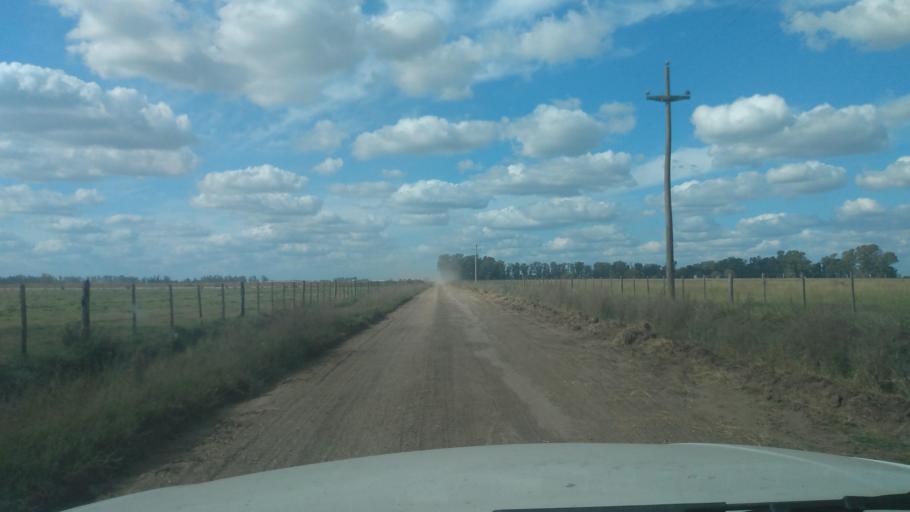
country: AR
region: Buenos Aires
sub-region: Partido de Navarro
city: Navarro
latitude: -35.0349
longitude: -59.5048
